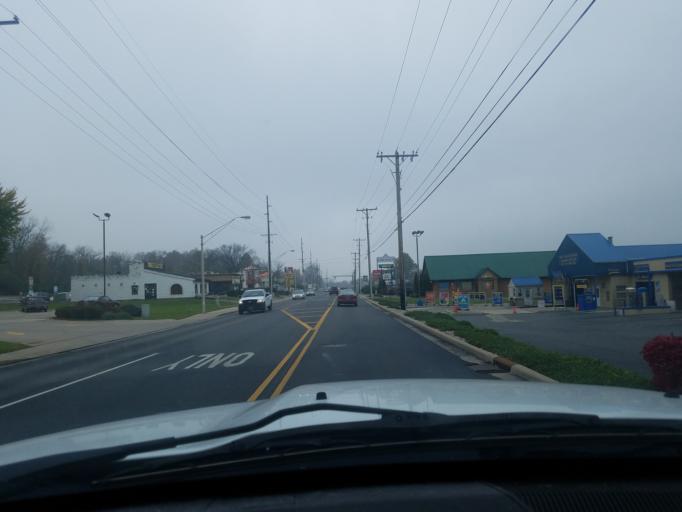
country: US
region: Indiana
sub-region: Cass County
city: Logansport
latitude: 40.7573
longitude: -86.3203
